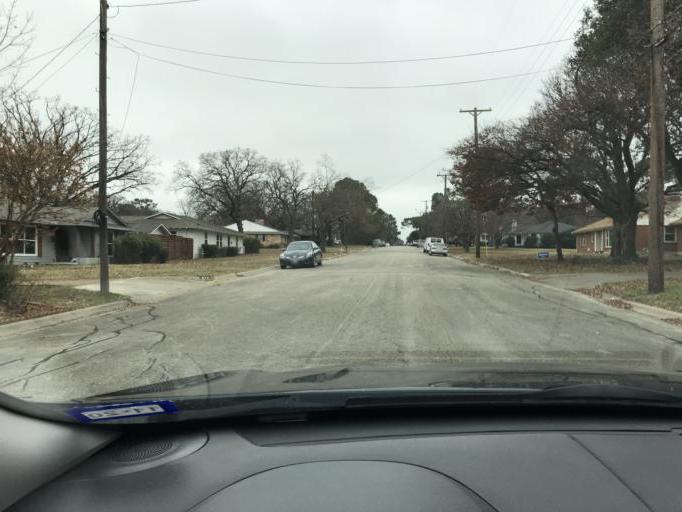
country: US
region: Texas
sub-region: Denton County
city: Denton
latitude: 33.2226
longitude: -97.1570
